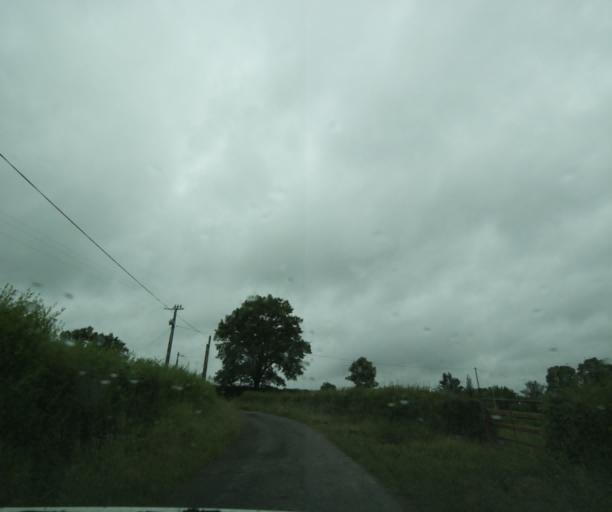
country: FR
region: Bourgogne
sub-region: Departement de Saone-et-Loire
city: Palinges
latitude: 46.4977
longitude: 4.2500
